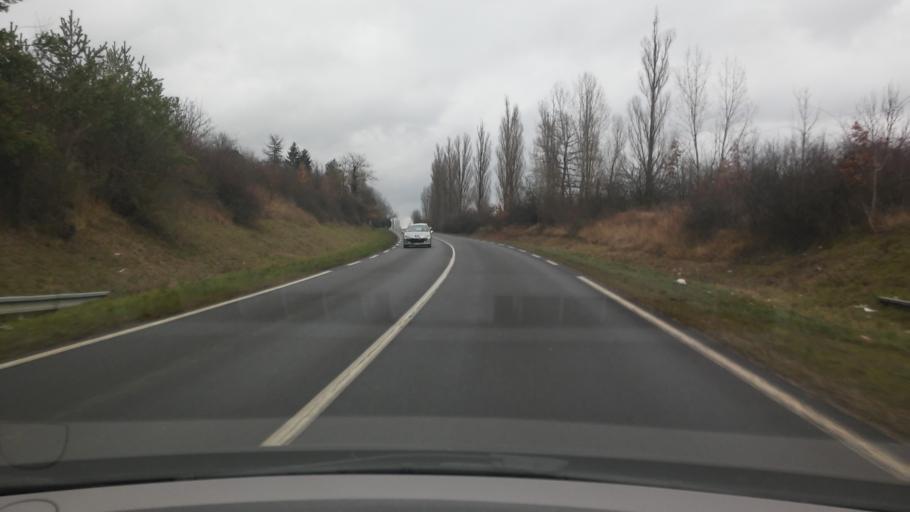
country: FR
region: Lorraine
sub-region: Departement de la Moselle
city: Retonfey
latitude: 49.1171
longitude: 6.2627
